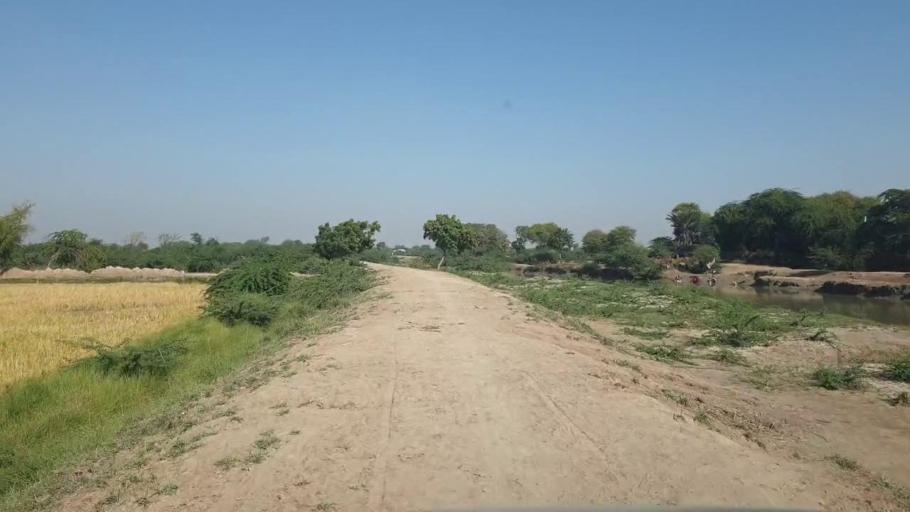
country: PK
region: Sindh
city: Talhar
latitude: 24.7862
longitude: 68.8084
